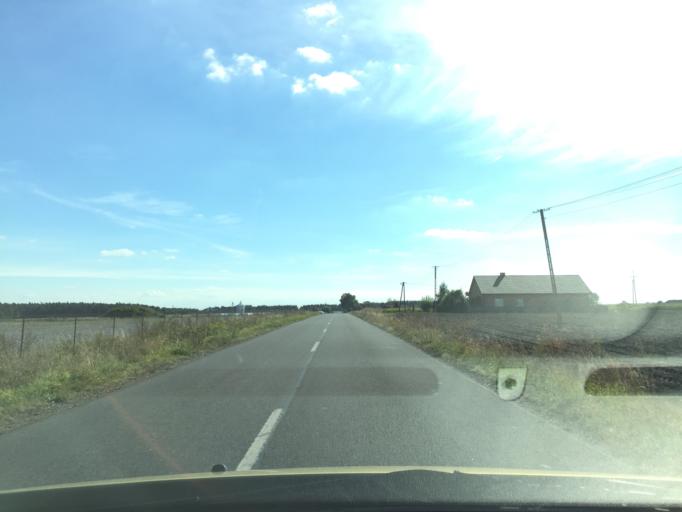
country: PL
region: Greater Poland Voivodeship
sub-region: Powiat kaliski
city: Stawiszyn
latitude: 51.9369
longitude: 18.1488
